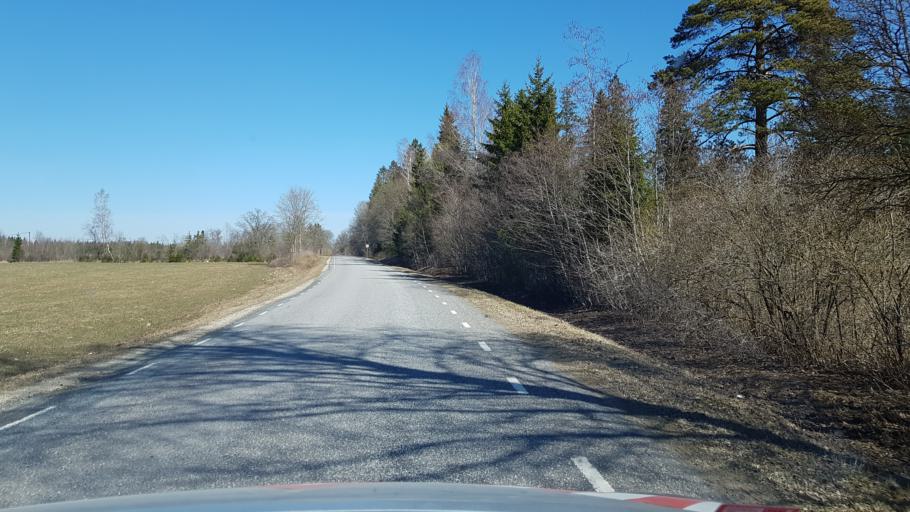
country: EE
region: Laeaene-Virumaa
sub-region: Tamsalu vald
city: Tamsalu
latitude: 59.0818
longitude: 26.1552
